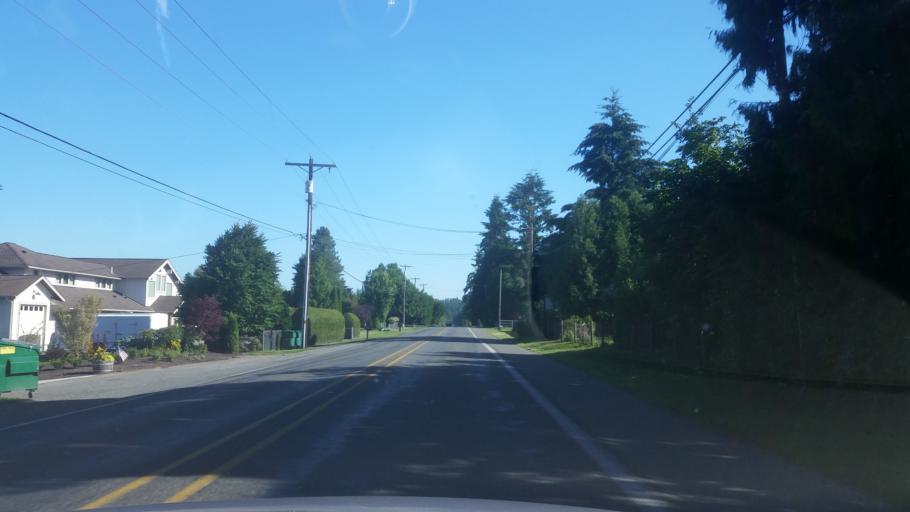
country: US
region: Washington
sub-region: Snohomish County
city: Cathcart
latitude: 47.8590
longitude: -122.0991
